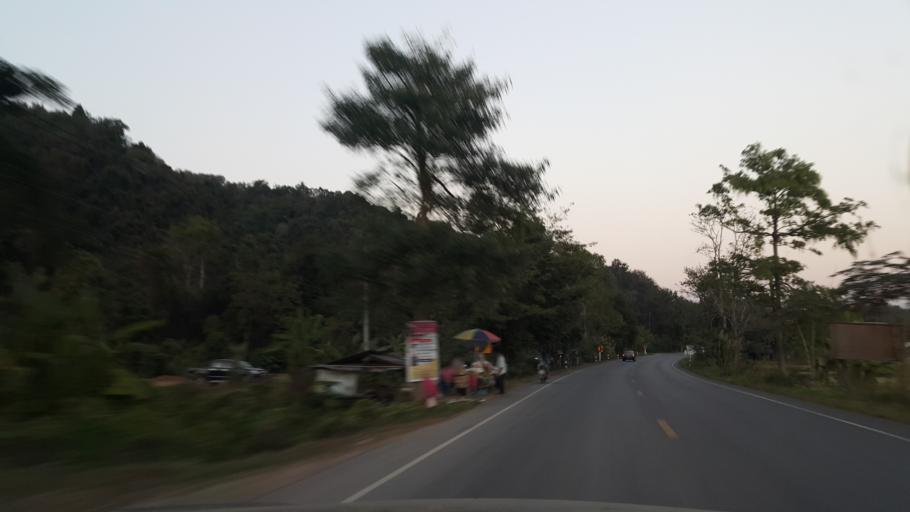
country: TH
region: Phrae
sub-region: Amphoe Wang Chin
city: Wang Chin
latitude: 17.9782
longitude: 99.6385
